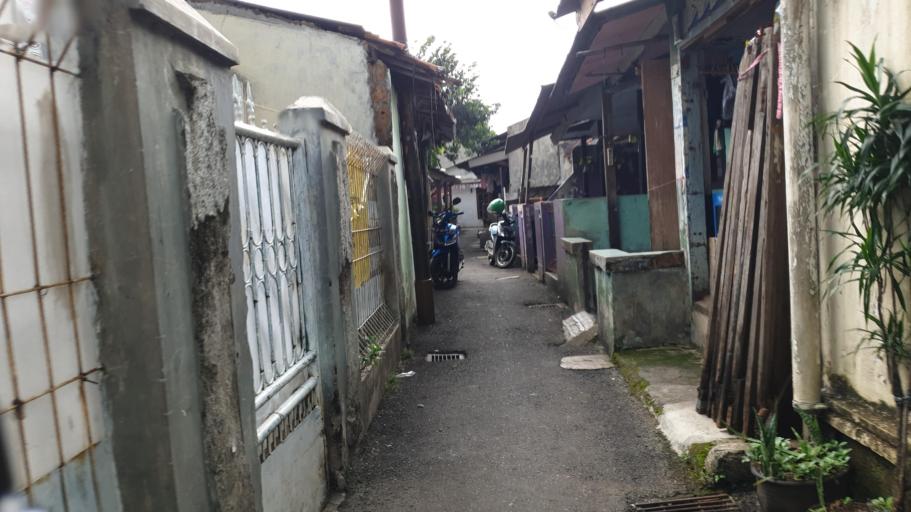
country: ID
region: West Java
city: Depok
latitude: -6.3367
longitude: 106.8215
